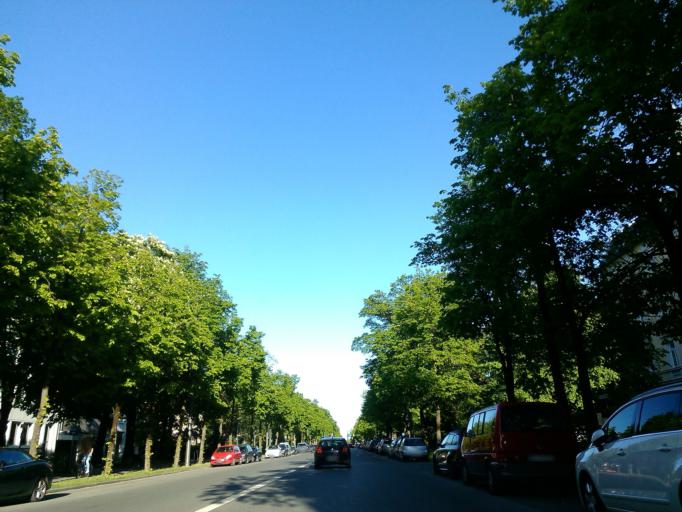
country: DE
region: Bavaria
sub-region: Upper Bavaria
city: Munich
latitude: 48.1508
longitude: 11.5414
